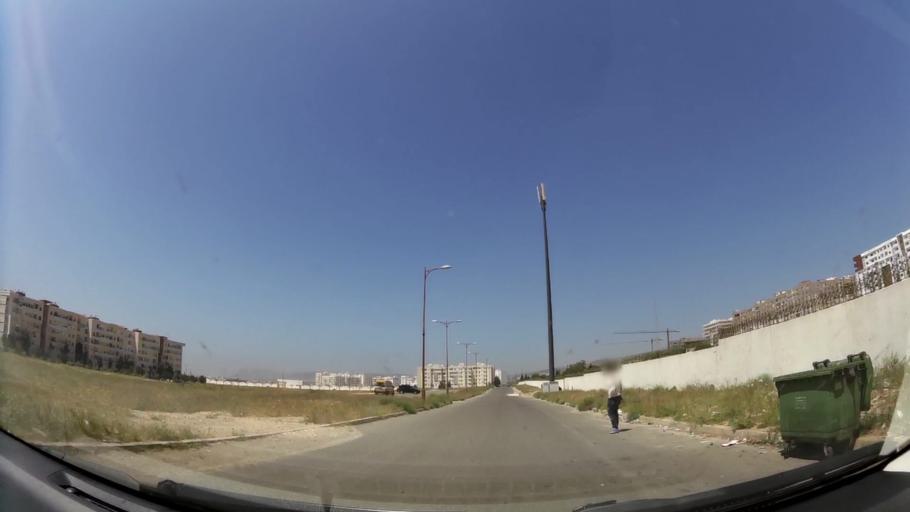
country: MA
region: Oued ed Dahab-Lagouira
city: Dakhla
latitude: 30.4330
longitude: -9.5628
